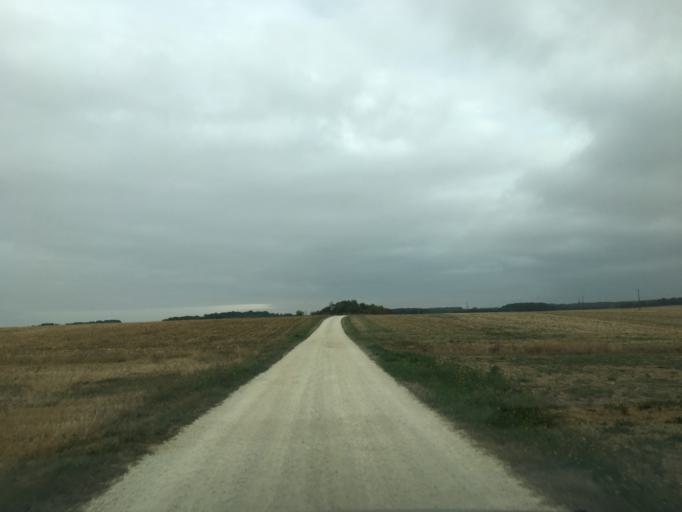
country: FR
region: Poitou-Charentes
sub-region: Departement des Deux-Sevres
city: Beauvoir-sur-Niort
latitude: 46.0824
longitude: -0.4927
